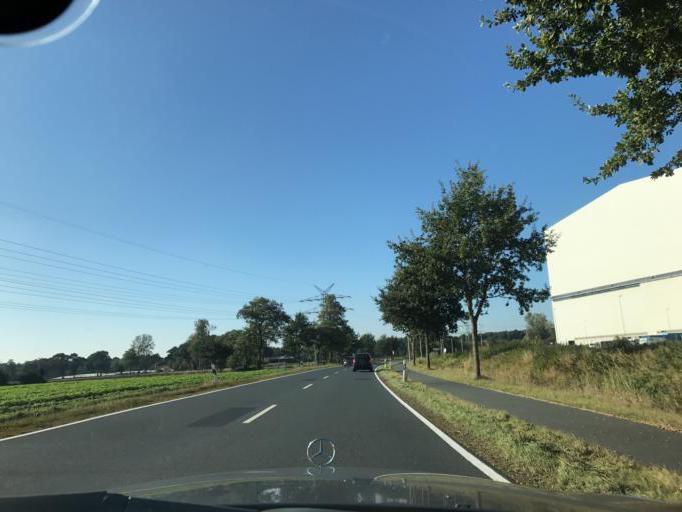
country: DE
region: Lower Saxony
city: Papenburg
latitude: 53.0925
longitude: 7.3610
